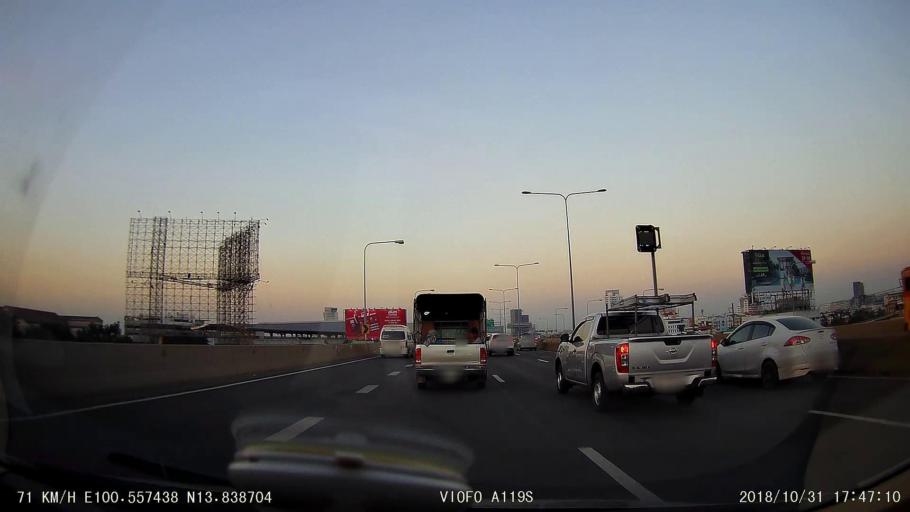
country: TH
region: Bangkok
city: Chatuchak
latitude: 13.8384
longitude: 100.5571
